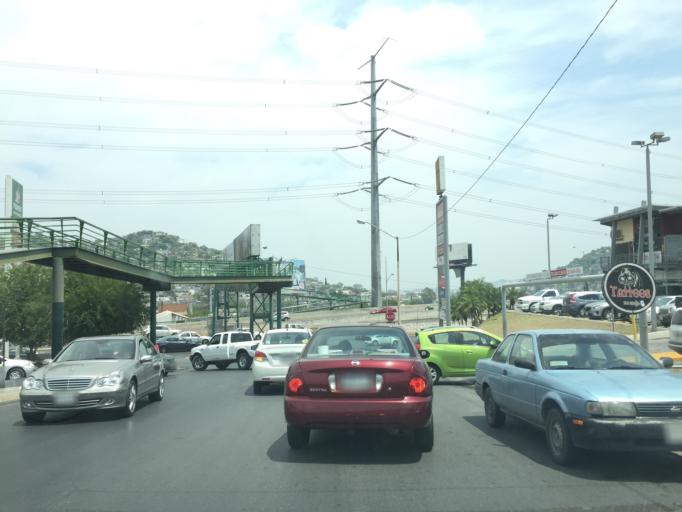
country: MX
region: Nuevo Leon
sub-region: Monterrey
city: Monterrey
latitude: 25.6372
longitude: -100.3122
